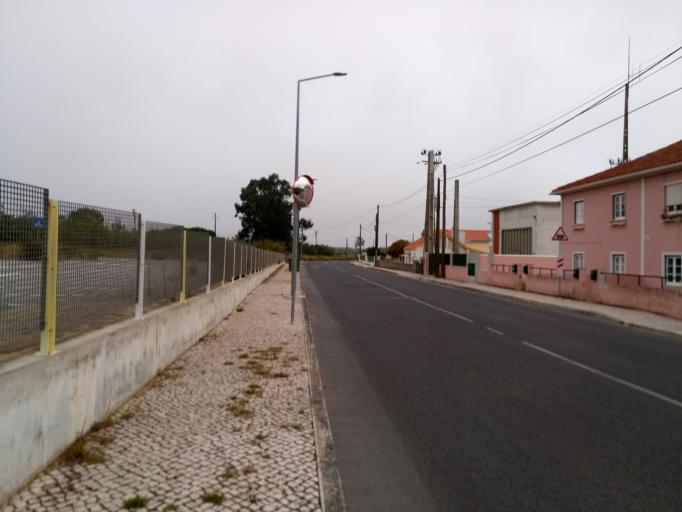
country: PT
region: Leiria
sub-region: Caldas da Rainha
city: Caldas da Rainha
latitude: 39.4154
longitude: -9.1415
